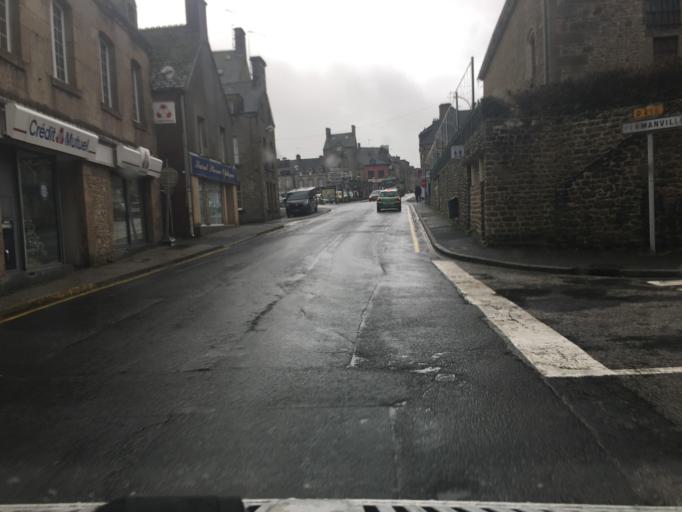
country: FR
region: Lower Normandy
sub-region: Departement de la Manche
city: Saint-Pierre-Eglise
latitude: 49.6691
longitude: -1.4052
